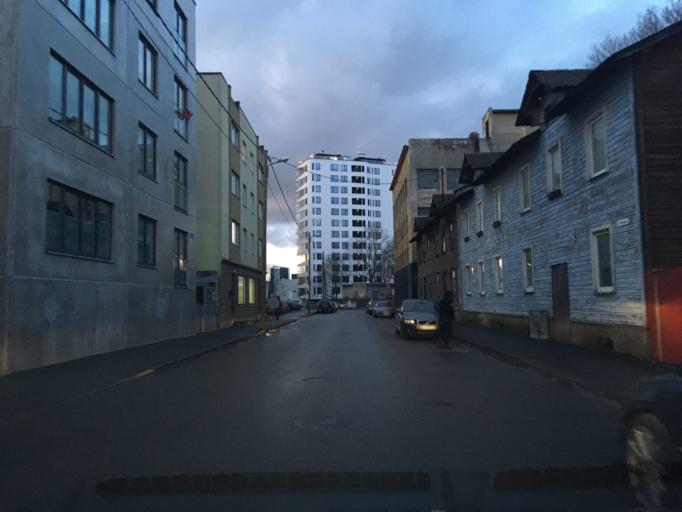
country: EE
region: Harju
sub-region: Tallinna linn
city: Tallinn
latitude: 59.4272
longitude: 24.7851
